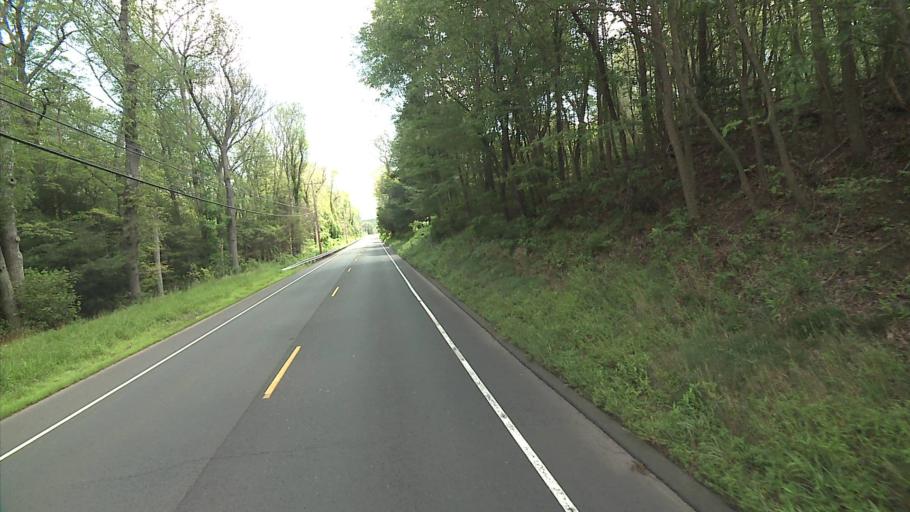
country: US
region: Connecticut
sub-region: Middlesex County
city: Higganum
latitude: 41.5026
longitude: -72.5716
